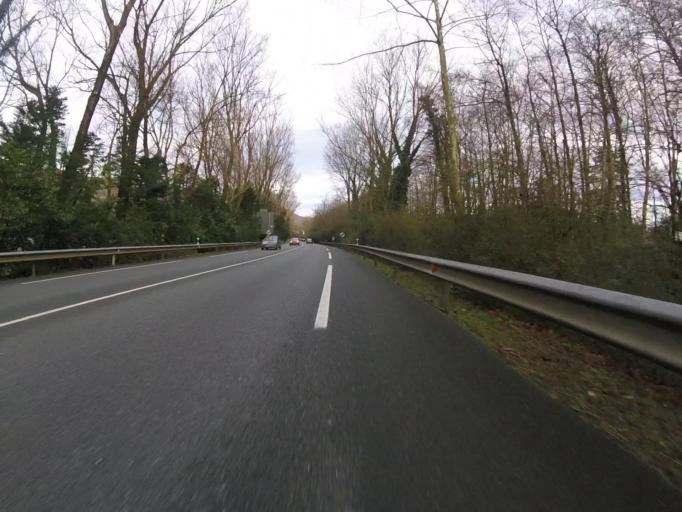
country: ES
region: Basque Country
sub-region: Provincia de Guipuzcoa
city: Irun
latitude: 43.3354
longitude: -1.8214
